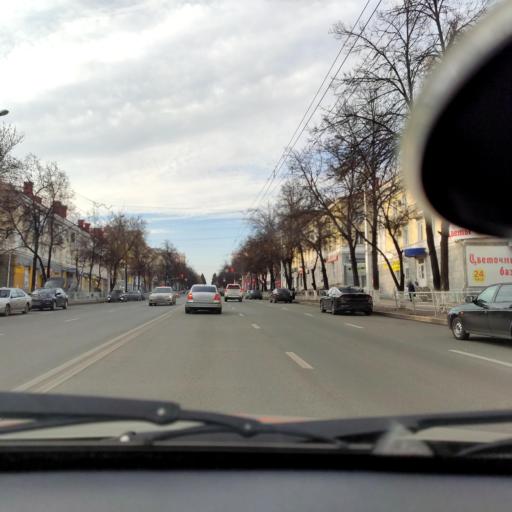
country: RU
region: Bashkortostan
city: Ufa
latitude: 54.8156
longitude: 56.0817
